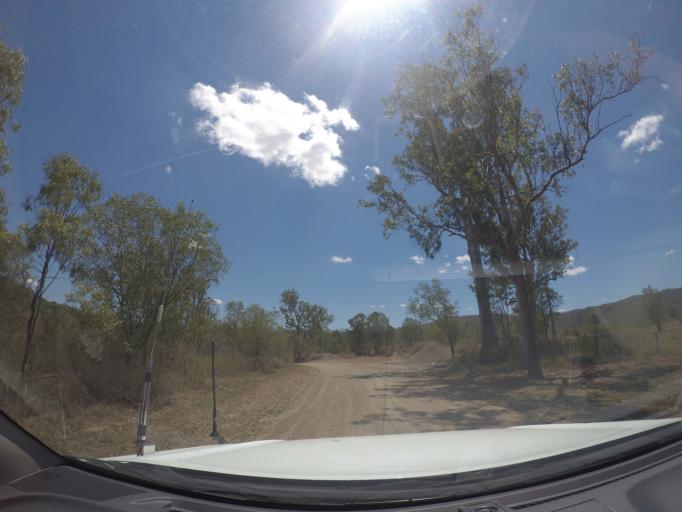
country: AU
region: Queensland
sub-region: Ipswich
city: Springfield Lakes
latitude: -27.8146
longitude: 152.8518
